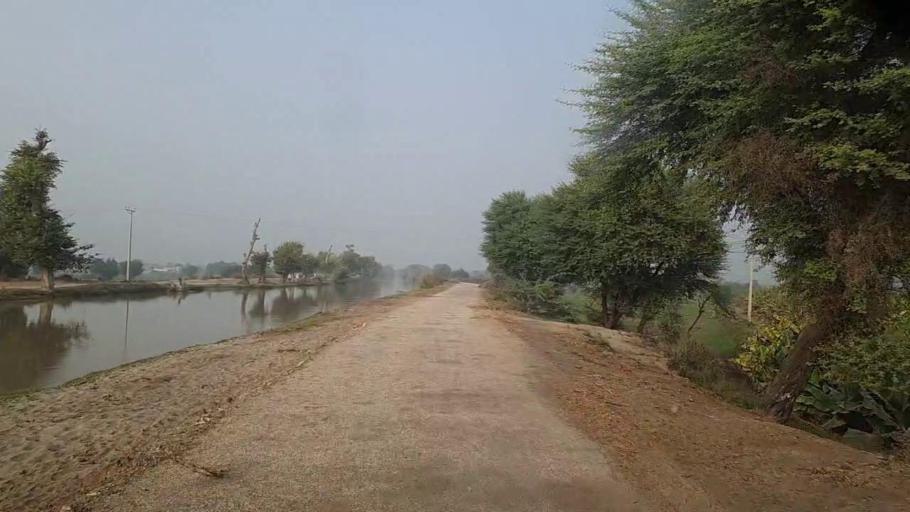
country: PK
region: Sindh
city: Bozdar
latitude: 27.1524
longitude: 68.6604
